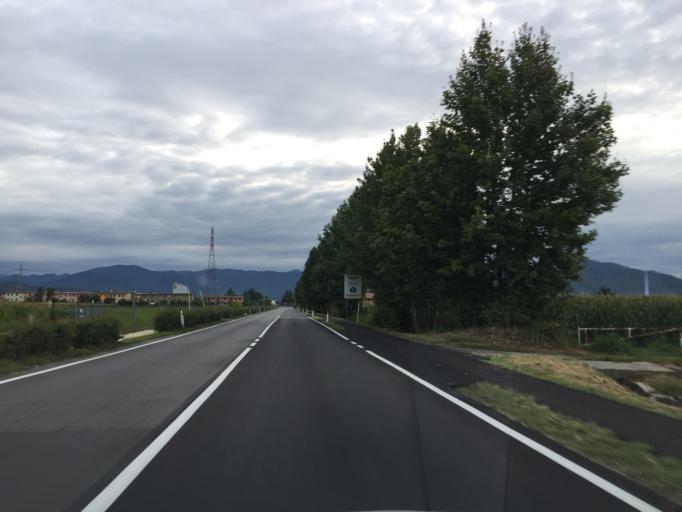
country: IT
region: Lombardy
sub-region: Provincia di Brescia
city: Folzano
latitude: 45.5022
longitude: 10.1881
